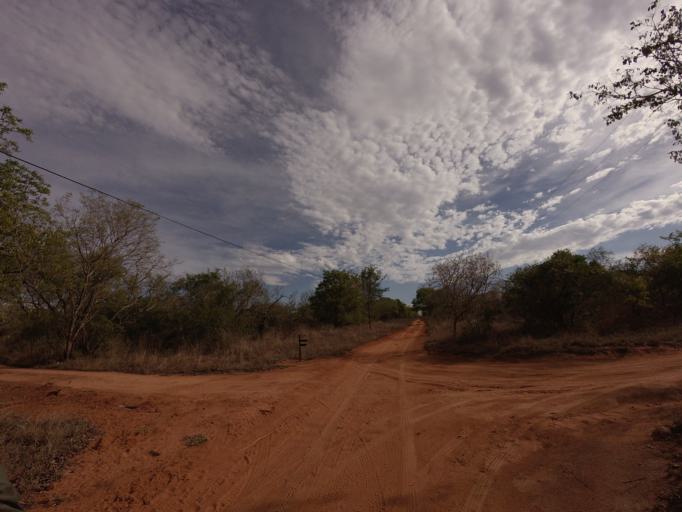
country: ZA
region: Limpopo
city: Thulamahashi
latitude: -24.5268
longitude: 31.1215
